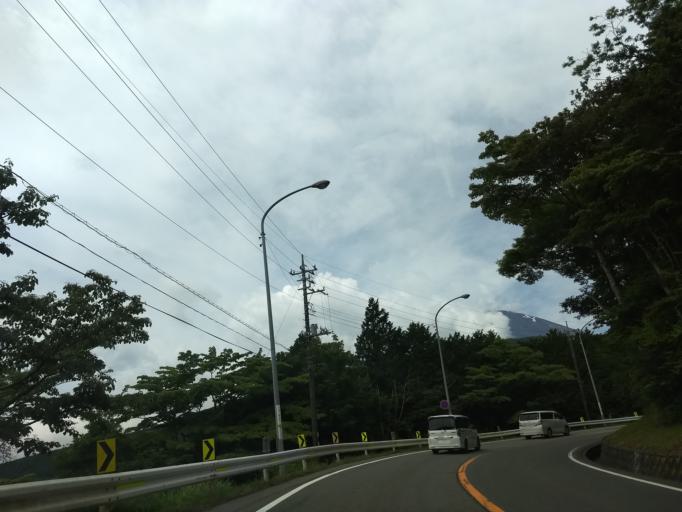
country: JP
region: Shizuoka
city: Gotemba
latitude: 35.3812
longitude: 138.8550
